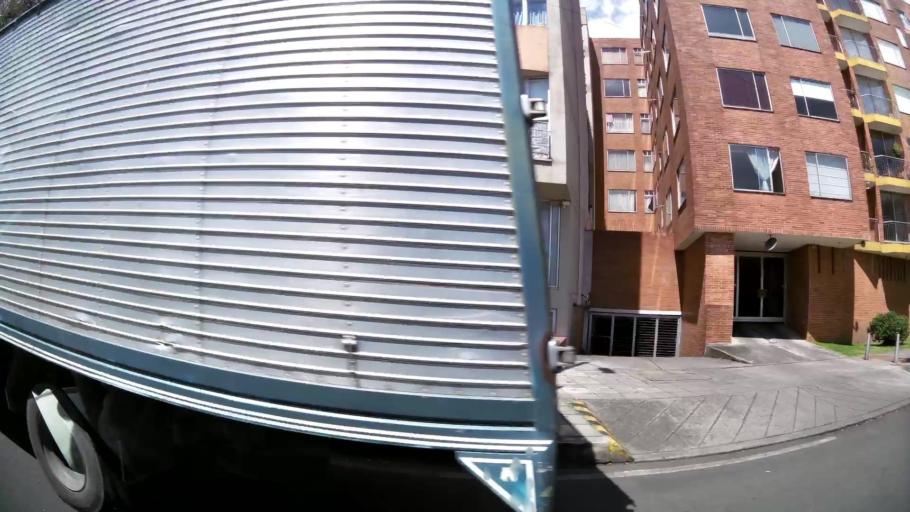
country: CO
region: Bogota D.C.
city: Bogota
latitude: 4.6335
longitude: -74.0987
